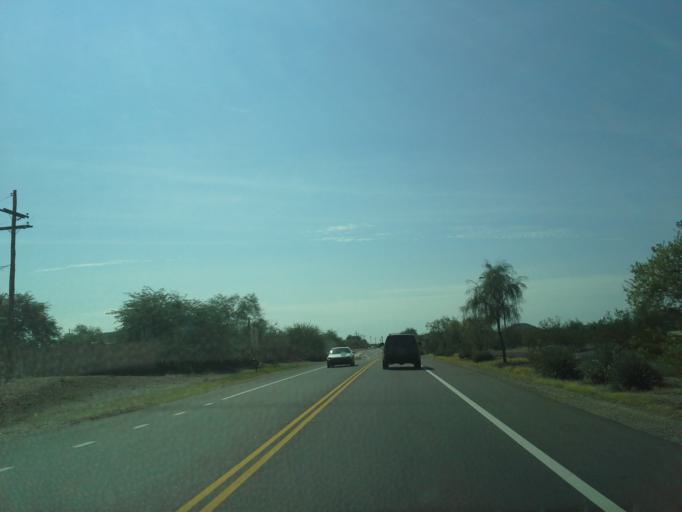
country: US
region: Arizona
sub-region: Pima County
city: Flowing Wells
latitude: 32.2454
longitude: -111.0204
